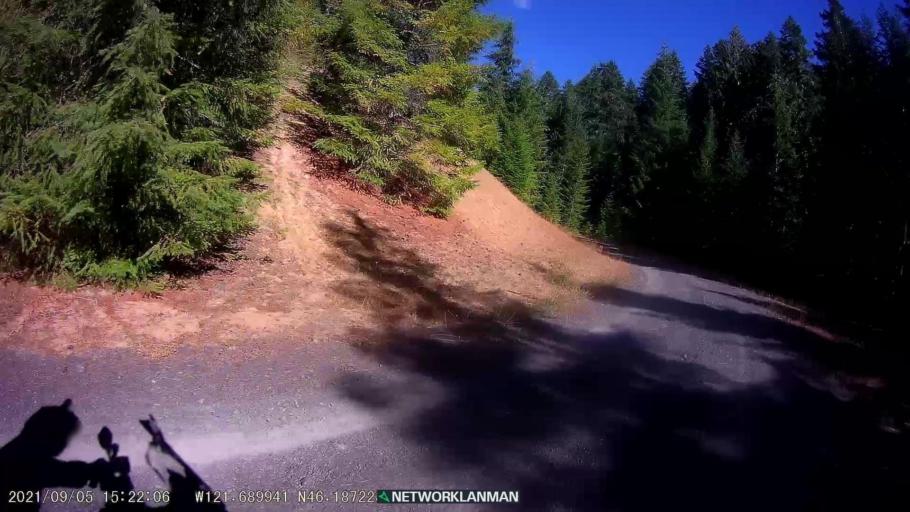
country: US
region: Washington
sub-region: Skamania County
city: Carson
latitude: 46.1871
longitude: -121.6899
